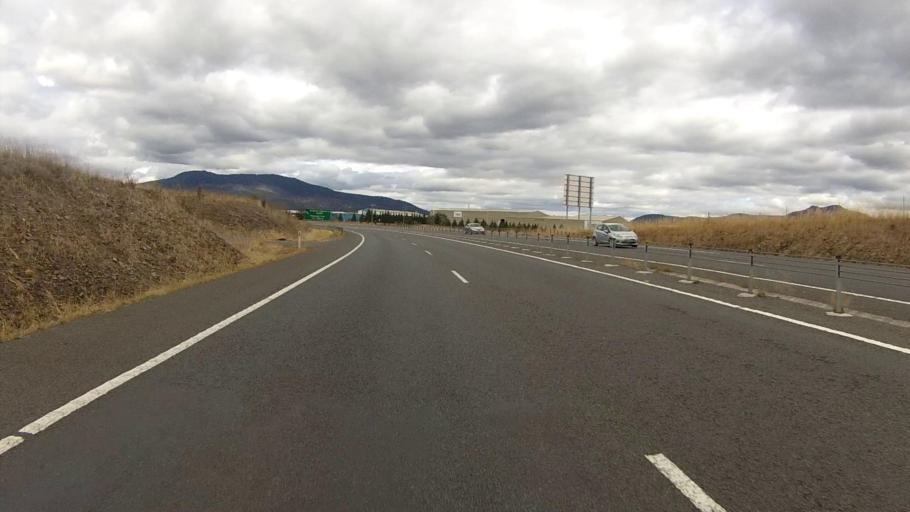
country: AU
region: Tasmania
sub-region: Brighton
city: Bridgewater
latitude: -42.7168
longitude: 147.2403
